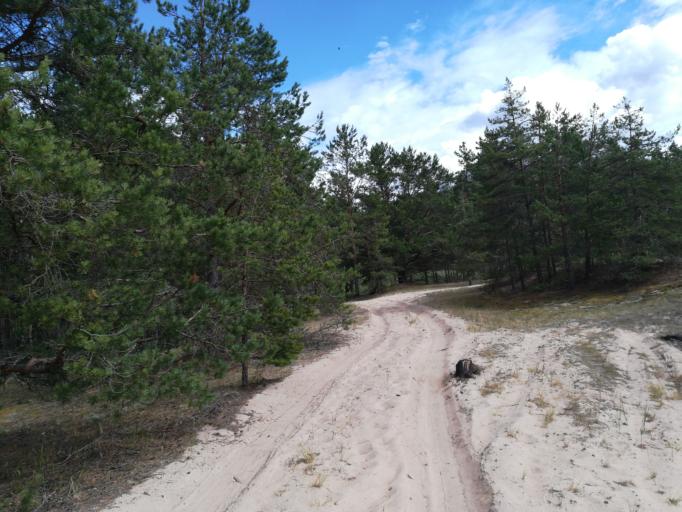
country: RU
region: Leningrad
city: Ust'-Luga
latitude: 59.6766
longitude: 28.2483
